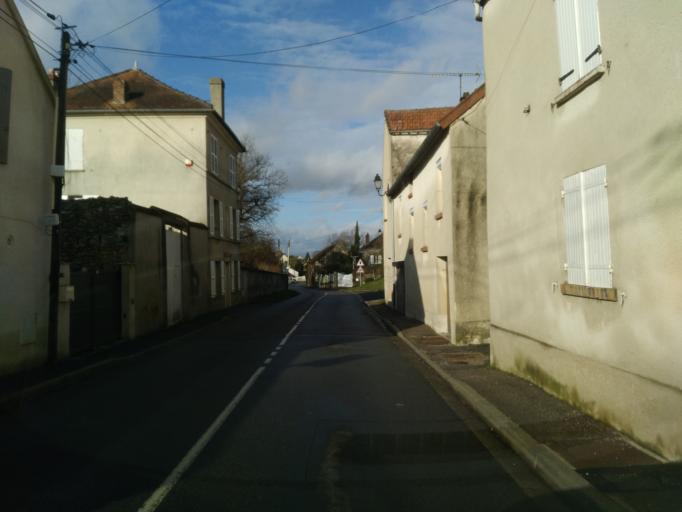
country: FR
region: Ile-de-France
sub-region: Departement des Yvelines
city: Bazemont
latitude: 48.9215
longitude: 1.8752
